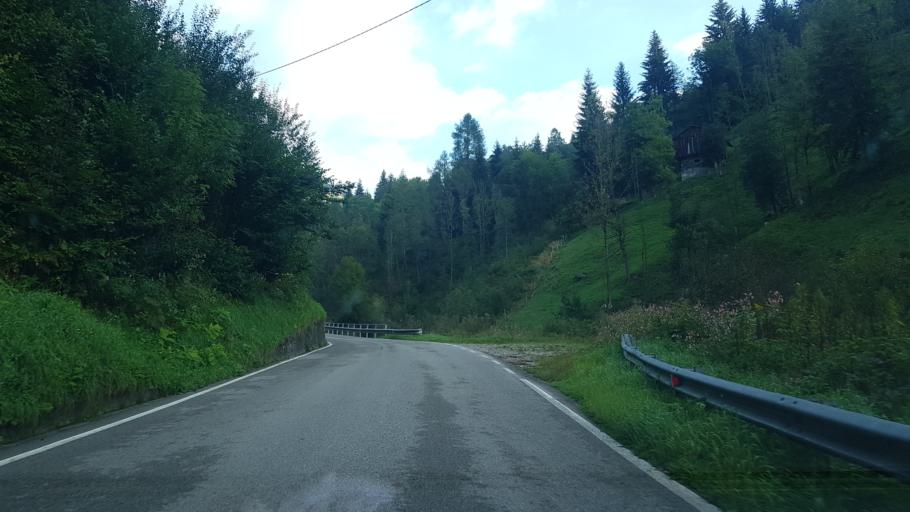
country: IT
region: Veneto
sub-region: Provincia di Belluno
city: San Pietro di Cadore
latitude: 46.5724
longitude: 12.5829
